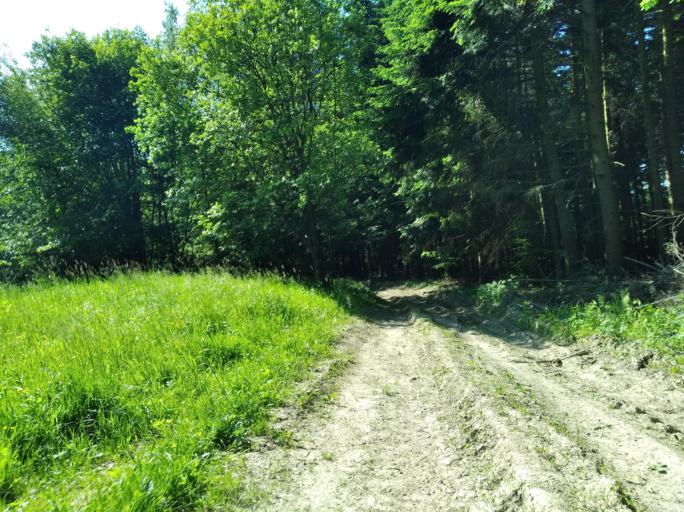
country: PL
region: Subcarpathian Voivodeship
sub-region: Powiat krosnienski
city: Odrzykon
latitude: 49.7684
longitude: 21.7508
